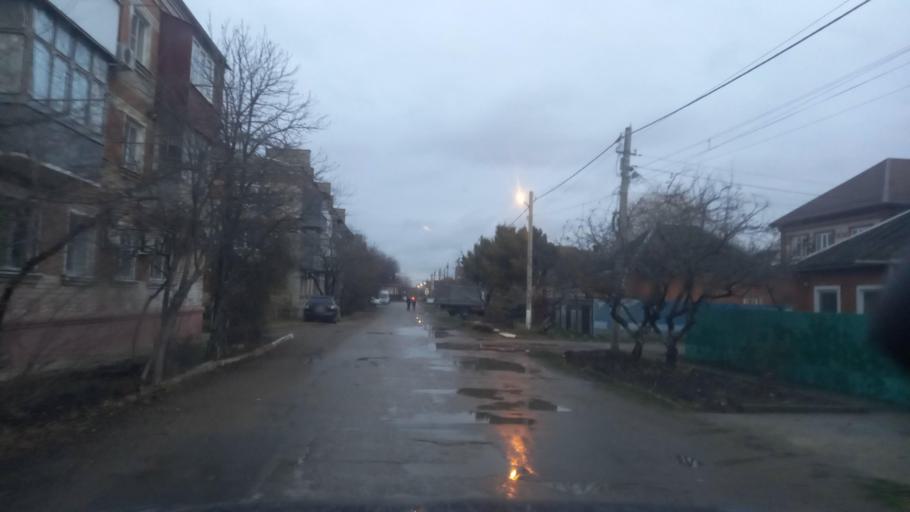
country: RU
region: Adygeya
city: Yablonovskiy
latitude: 44.9777
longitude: 38.9366
